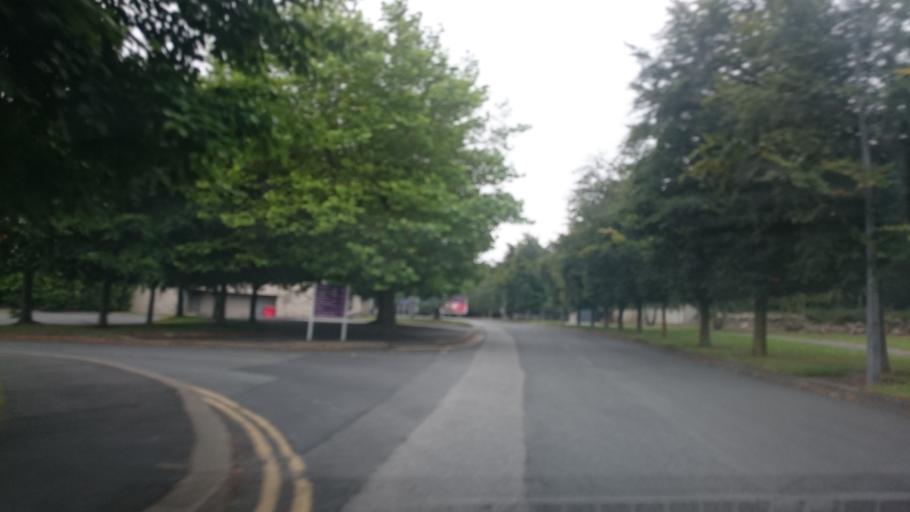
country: IE
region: Leinster
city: Foxrock
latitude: 53.2679
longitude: -6.1949
